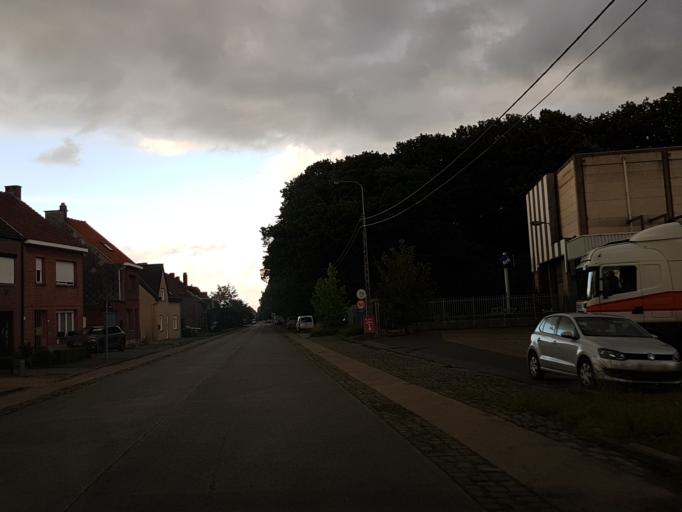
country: BE
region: Flanders
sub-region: Provincie Oost-Vlaanderen
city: Buggenhout
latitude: 51.0043
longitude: 4.2040
